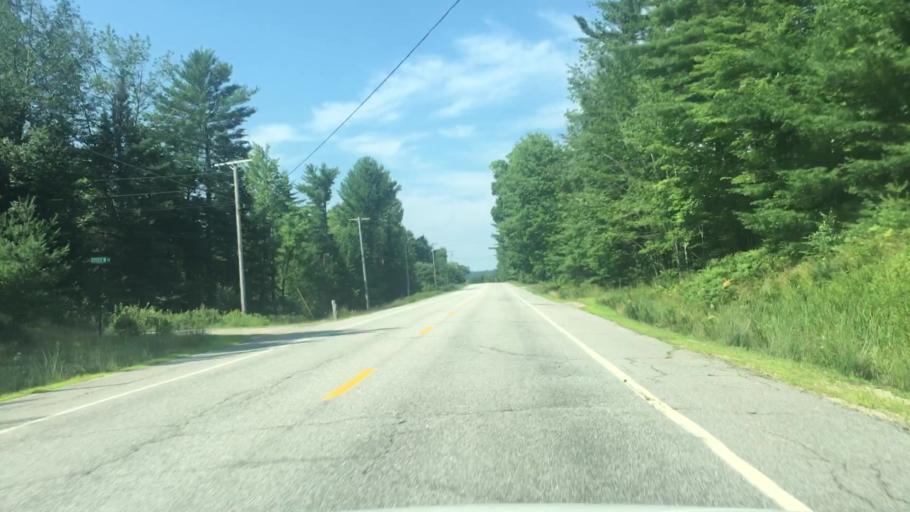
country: US
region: Maine
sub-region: Oxford County
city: West Paris
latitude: 44.3358
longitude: -70.5388
